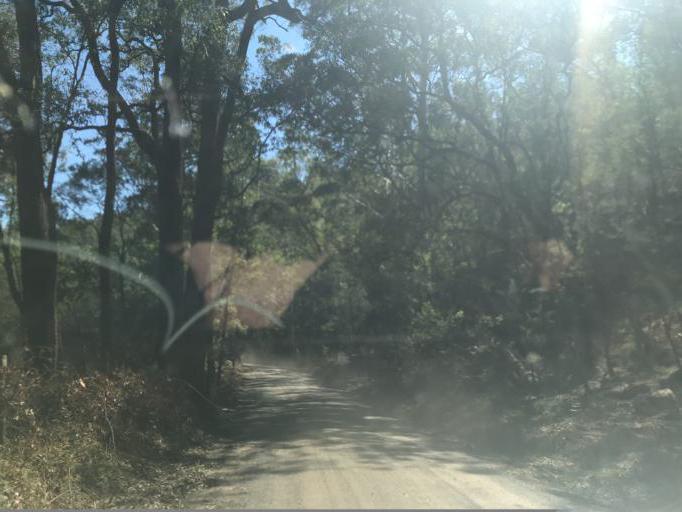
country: AU
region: New South Wales
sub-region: Wyong Shire
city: Little Jilliby
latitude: -33.1978
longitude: 151.0218
